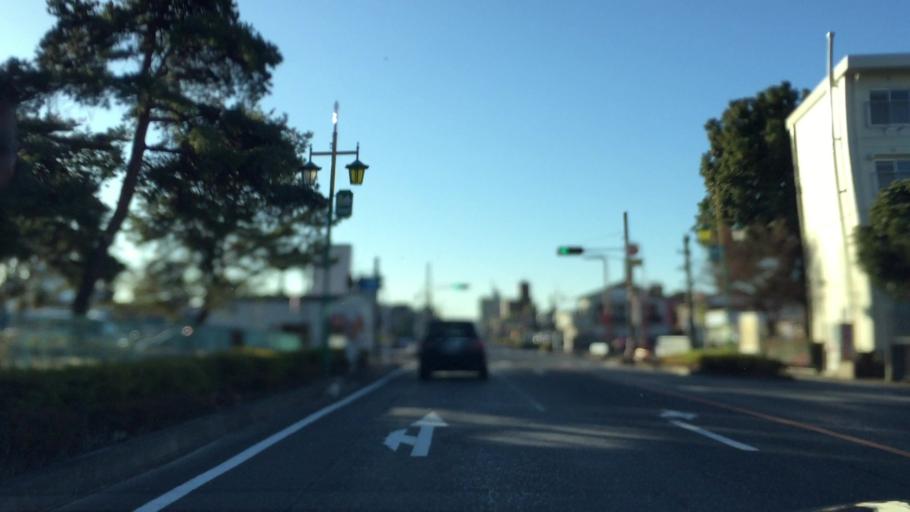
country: JP
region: Saitama
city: Menuma
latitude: 36.2635
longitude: 139.4066
